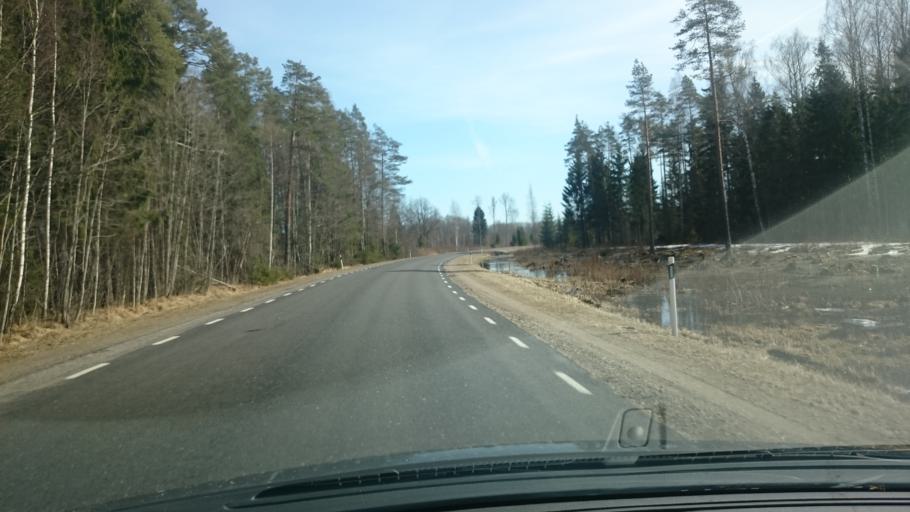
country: EE
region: Paernumaa
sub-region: Tootsi vald
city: Tootsi
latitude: 58.6410
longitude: 24.9009
